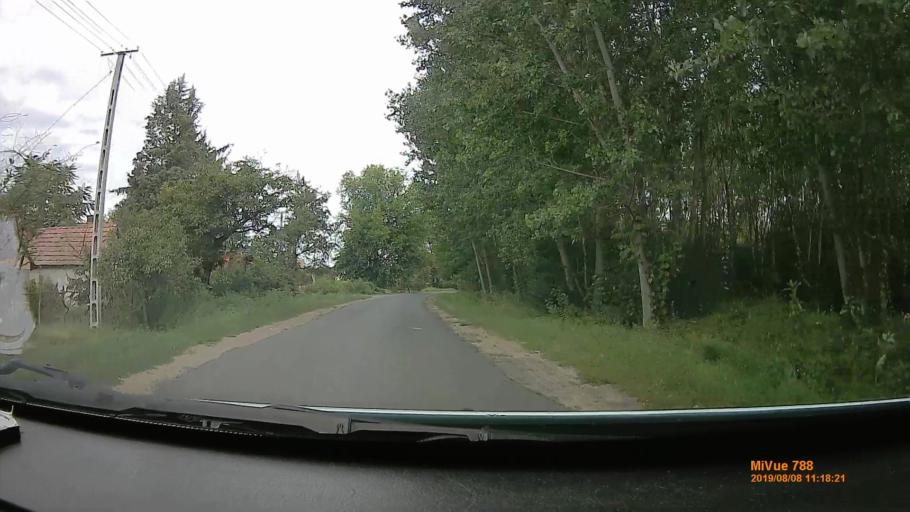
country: HU
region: Szabolcs-Szatmar-Bereg
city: Balkany
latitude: 47.7371
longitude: 21.8363
